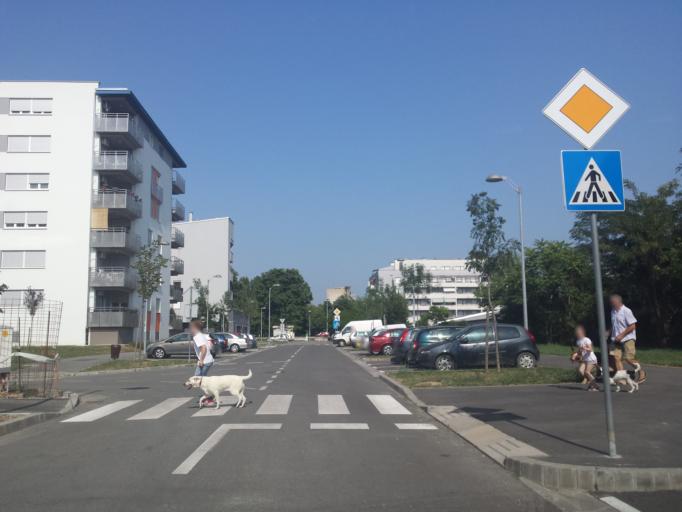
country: HR
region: Grad Zagreb
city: Zagreb - Centar
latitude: 45.8018
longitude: 15.9410
